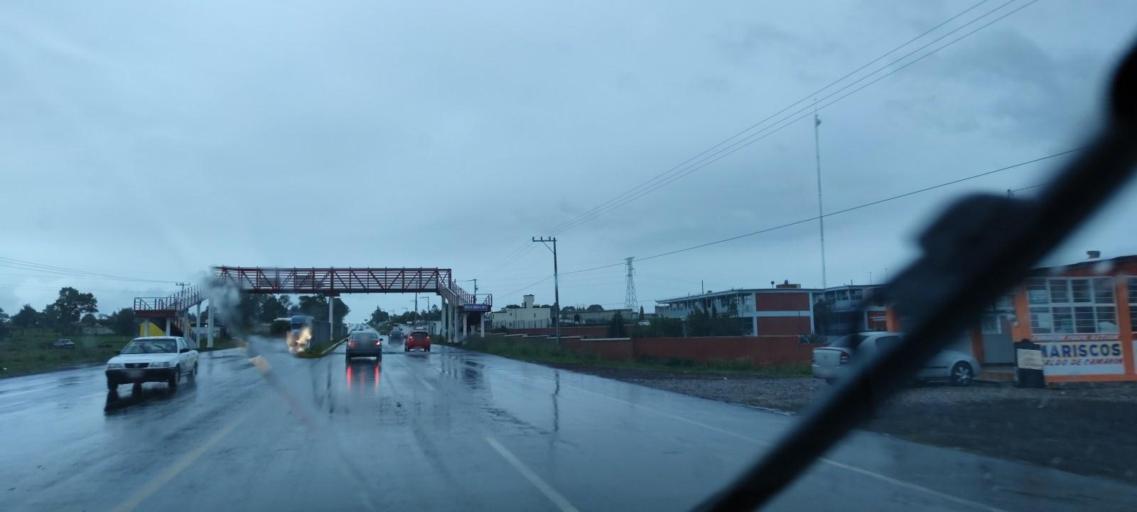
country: MX
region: Mexico
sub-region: Jilotepec
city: Doxhicho
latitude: 19.9208
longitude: -99.5917
